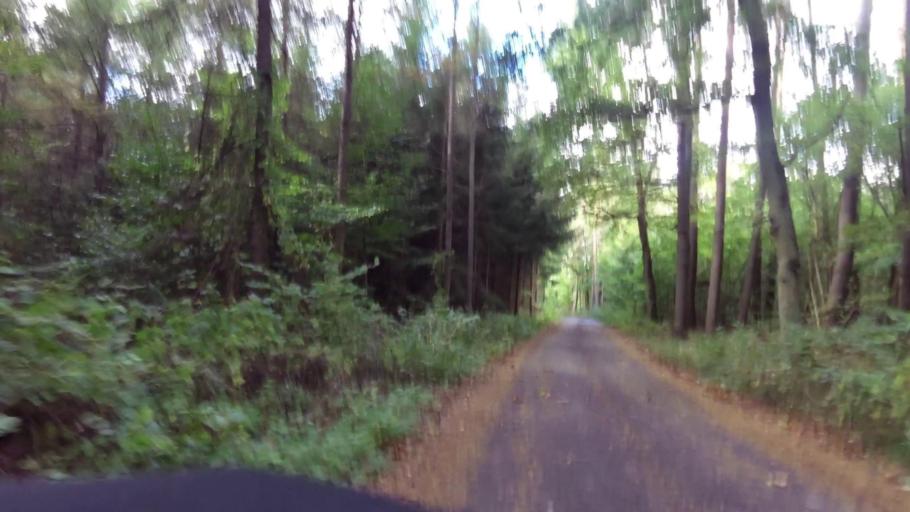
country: PL
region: West Pomeranian Voivodeship
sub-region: Powiat bialogardzki
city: Bialogard
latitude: 54.0577
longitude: 16.1214
